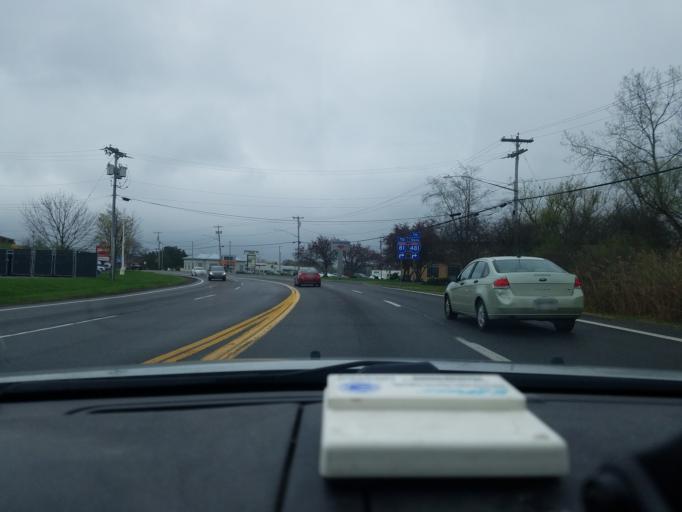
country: US
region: New York
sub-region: Onondaga County
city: North Syracuse
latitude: 43.1481
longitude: -76.1211
